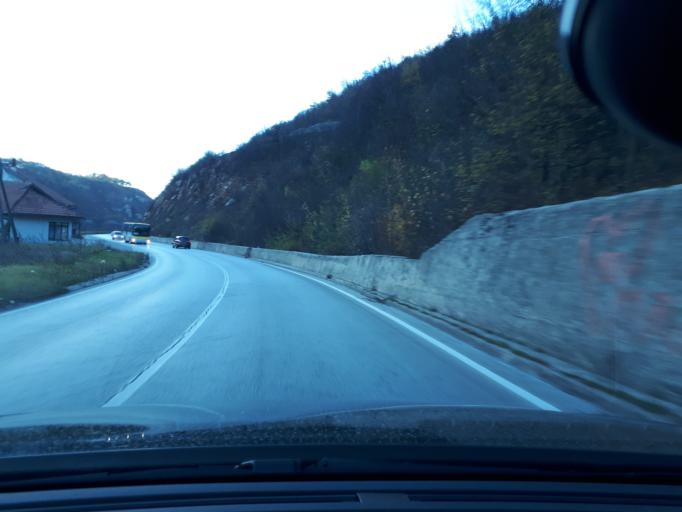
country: BA
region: Republika Srpska
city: Pale
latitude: 43.8435
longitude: 18.4776
